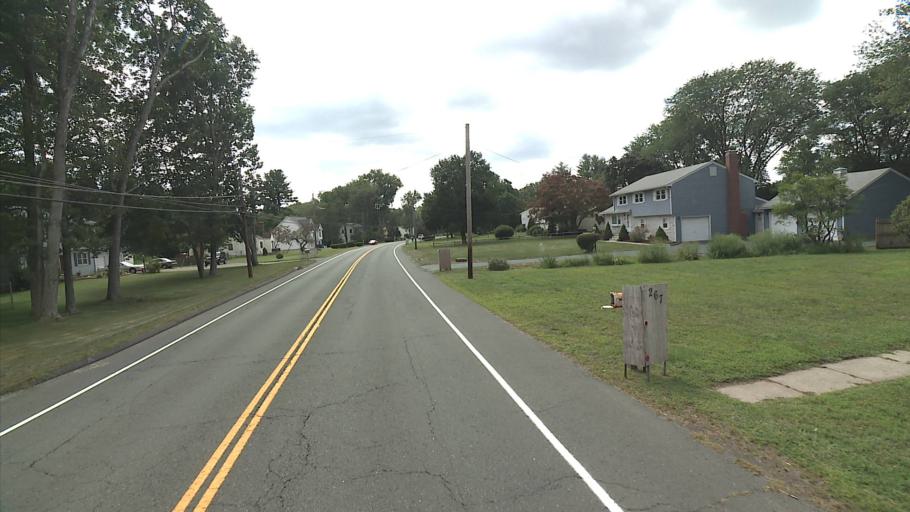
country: US
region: Connecticut
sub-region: Hartford County
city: Tariffville
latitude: 41.8566
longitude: -72.7409
